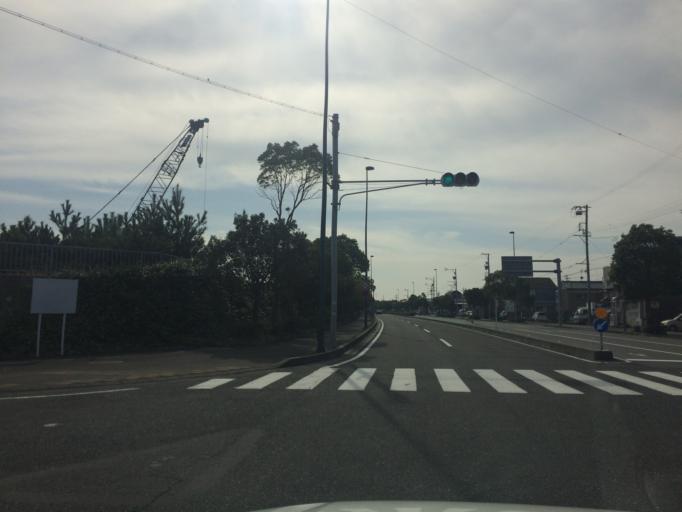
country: JP
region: Shizuoka
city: Yaizu
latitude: 34.8630
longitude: 138.3250
